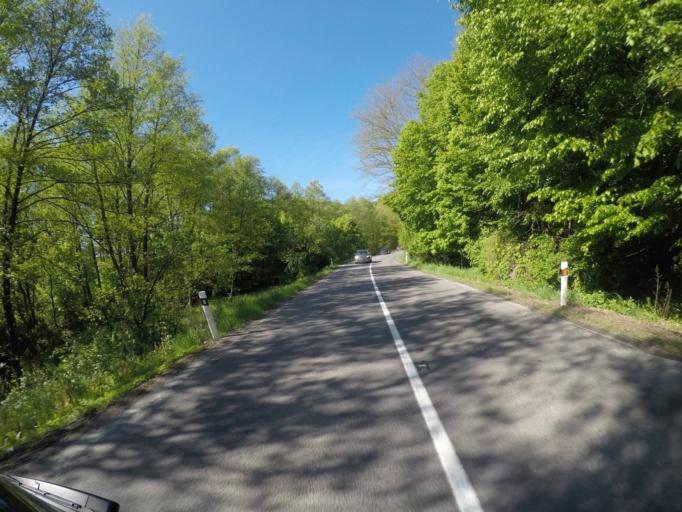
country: SK
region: Banskobystricky
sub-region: Okres Banska Bystrica
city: Banska Stiavnica
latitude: 48.5605
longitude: 19.0063
